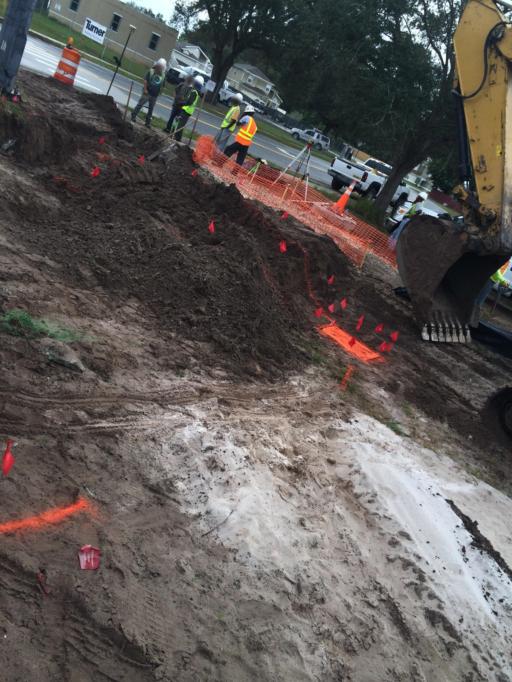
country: US
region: Florida
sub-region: Osceola County
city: Buenaventura Lakes
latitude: 28.3425
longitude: -81.3518
